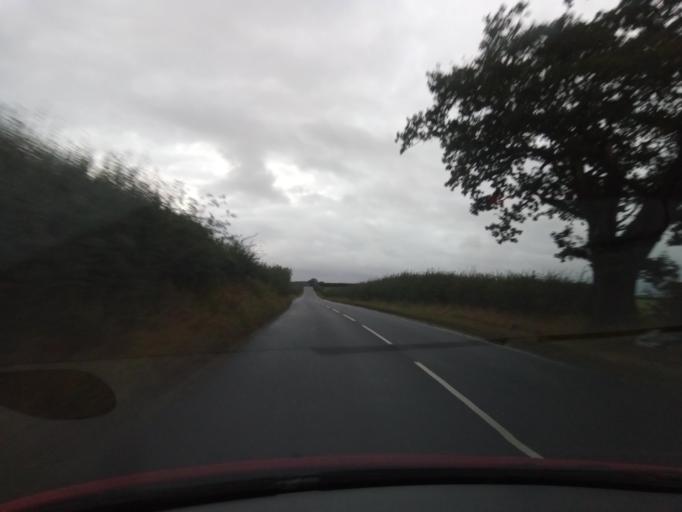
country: GB
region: England
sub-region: Darlington
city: Denton
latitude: 54.5573
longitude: -1.6755
